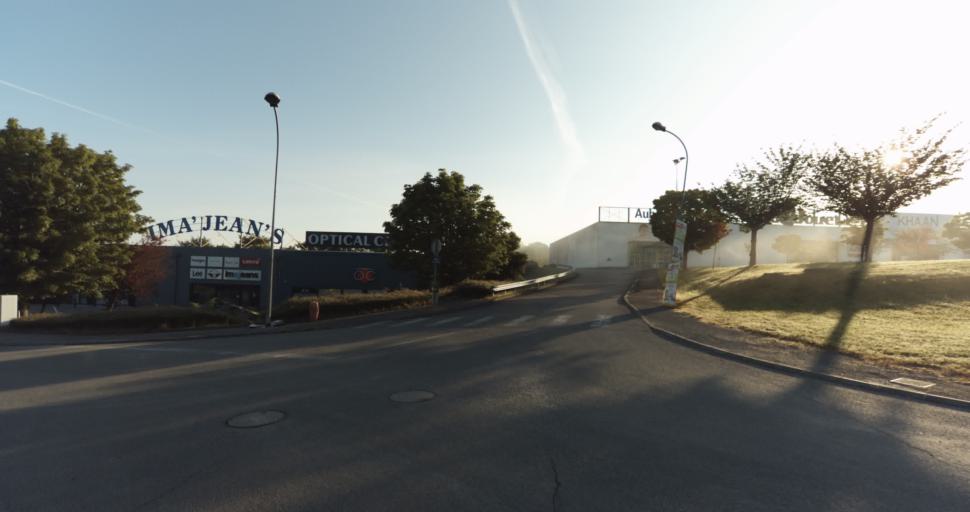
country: FR
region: Limousin
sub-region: Departement de la Haute-Vienne
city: Condat-sur-Vienne
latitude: 45.7800
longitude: 1.3095
